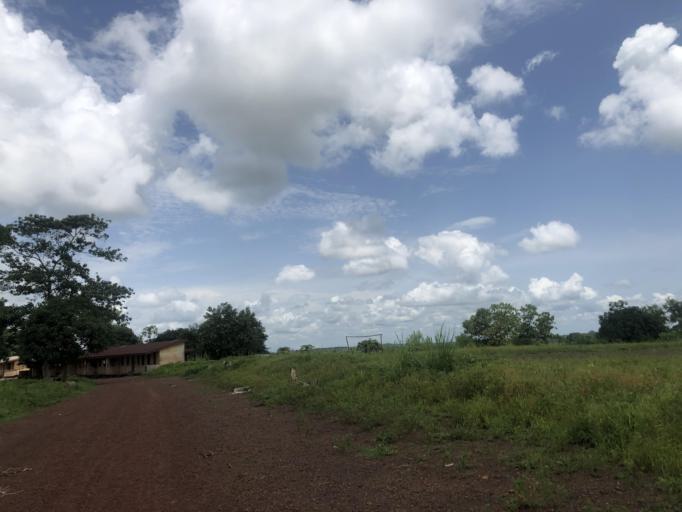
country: SL
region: Northern Province
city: Magburaka
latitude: 8.6895
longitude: -11.9452
